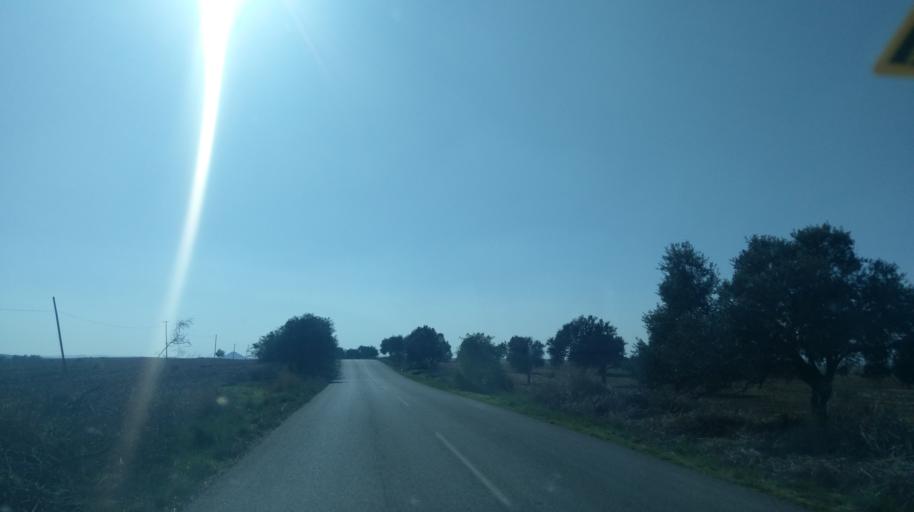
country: CY
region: Larnaka
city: Athienou
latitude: 35.1156
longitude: 33.5008
